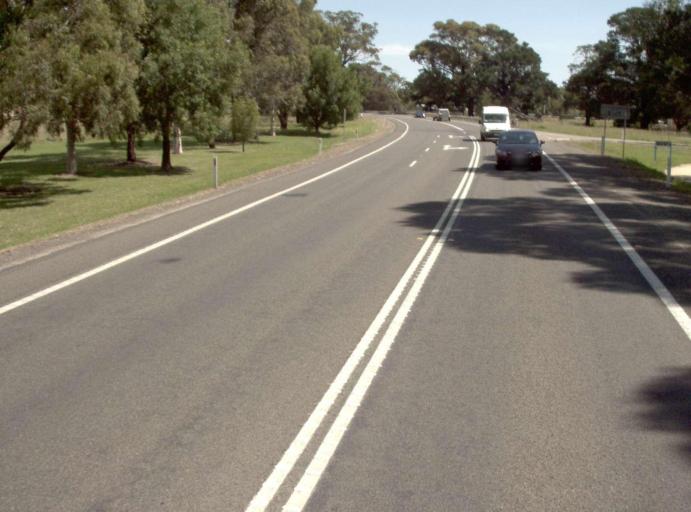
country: AU
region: Victoria
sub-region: Wellington
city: Sale
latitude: -37.9754
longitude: 147.0742
